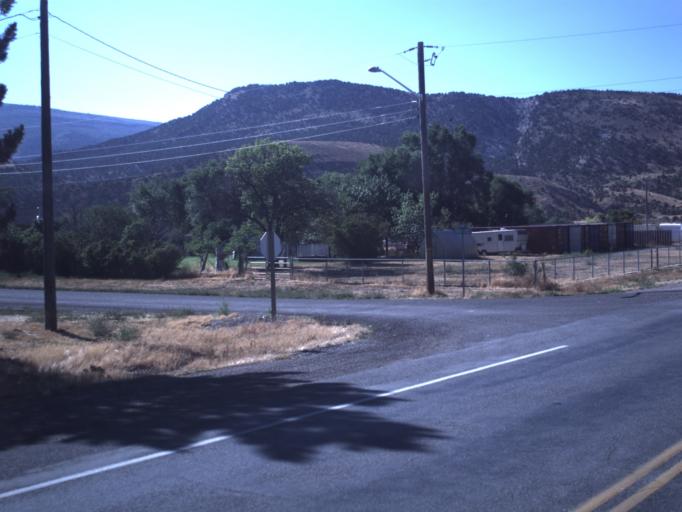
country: US
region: Utah
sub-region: Sanpete County
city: Manti
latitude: 39.1937
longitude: -111.6926
